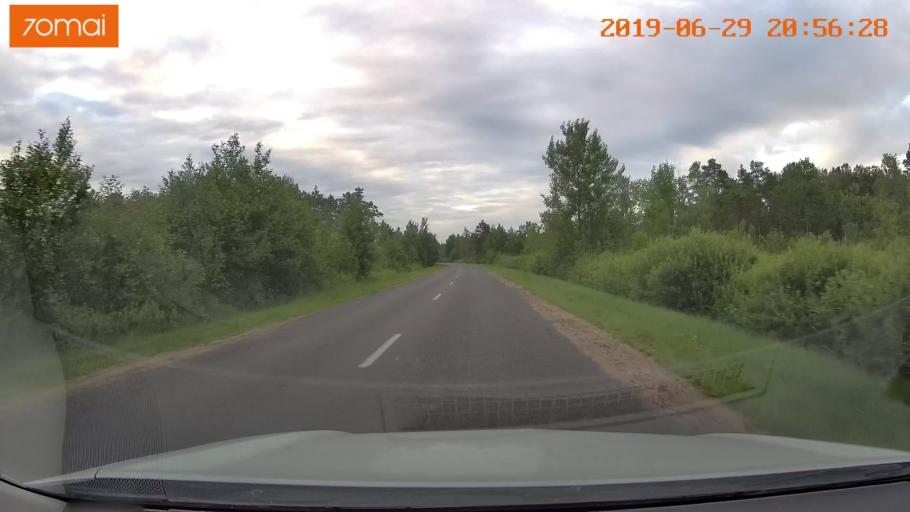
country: BY
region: Brest
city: Hantsavichy
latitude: 52.7057
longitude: 26.3678
